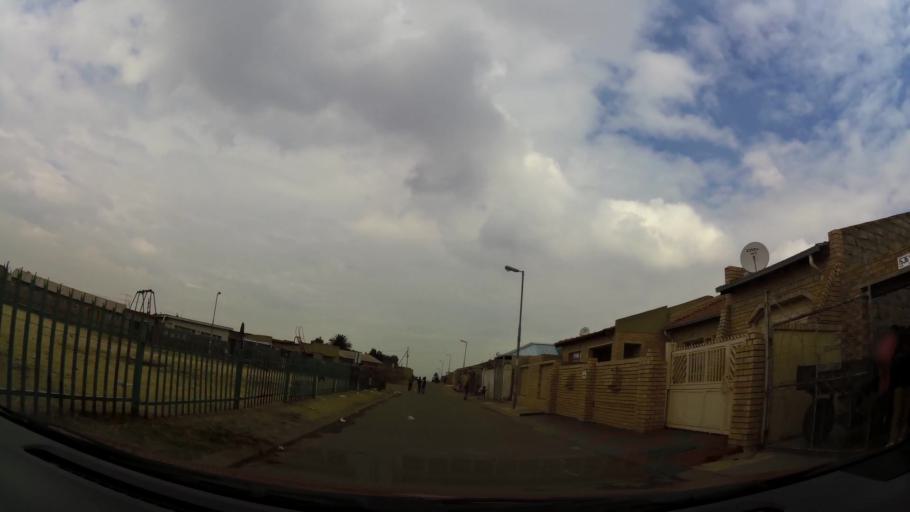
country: ZA
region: Gauteng
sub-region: City of Johannesburg Metropolitan Municipality
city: Soweto
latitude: -26.2543
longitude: 27.8271
